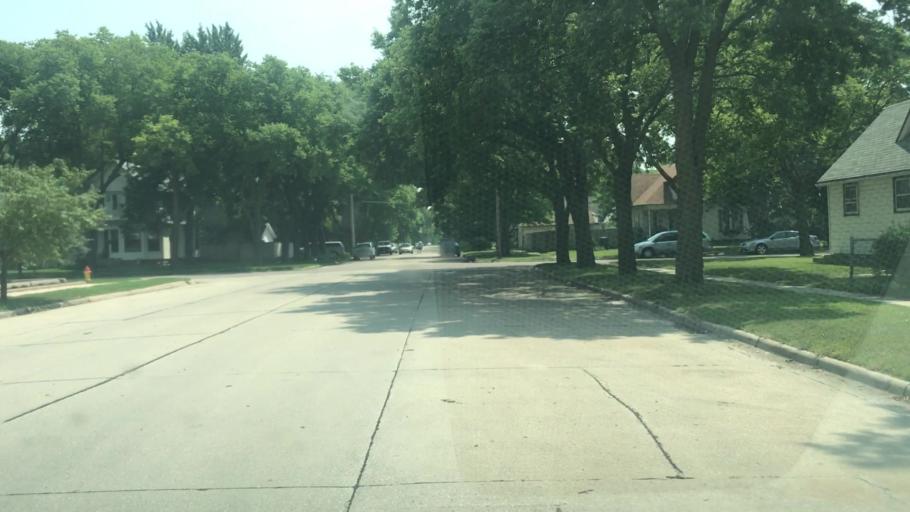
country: US
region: Nebraska
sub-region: Hall County
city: Grand Island
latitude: 40.9196
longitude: -98.3512
